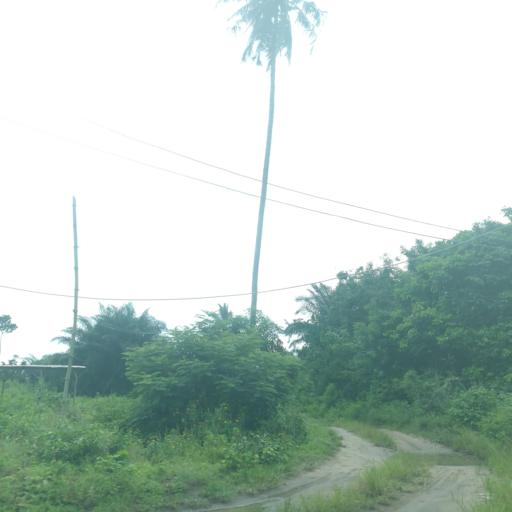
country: NG
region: Lagos
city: Ejirin
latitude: 6.6204
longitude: 3.7053
